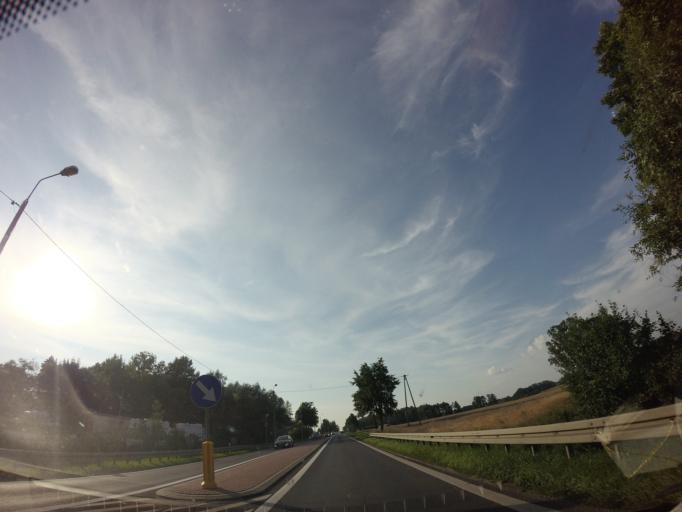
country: PL
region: Podlasie
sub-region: Powiat sokolski
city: Suchowola
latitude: 53.4467
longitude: 23.0924
